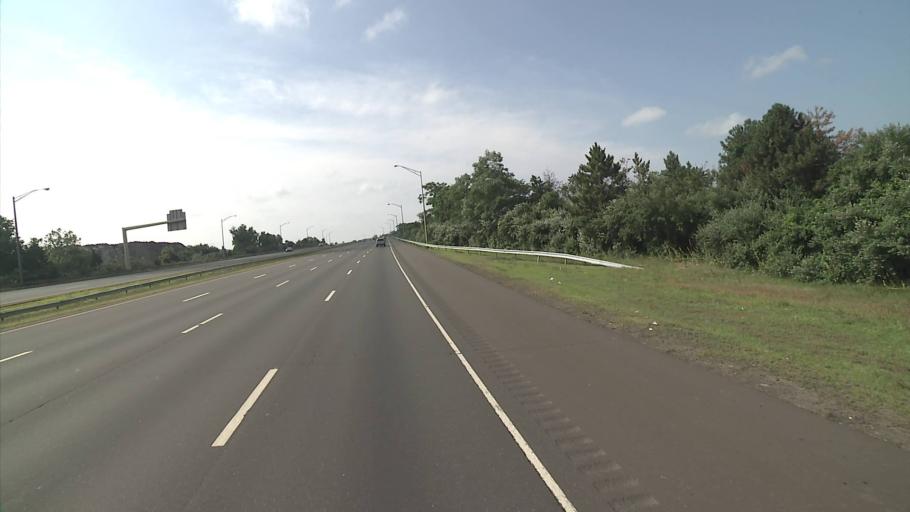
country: US
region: Connecticut
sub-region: New Haven County
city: North Haven
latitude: 41.3590
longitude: -72.8683
